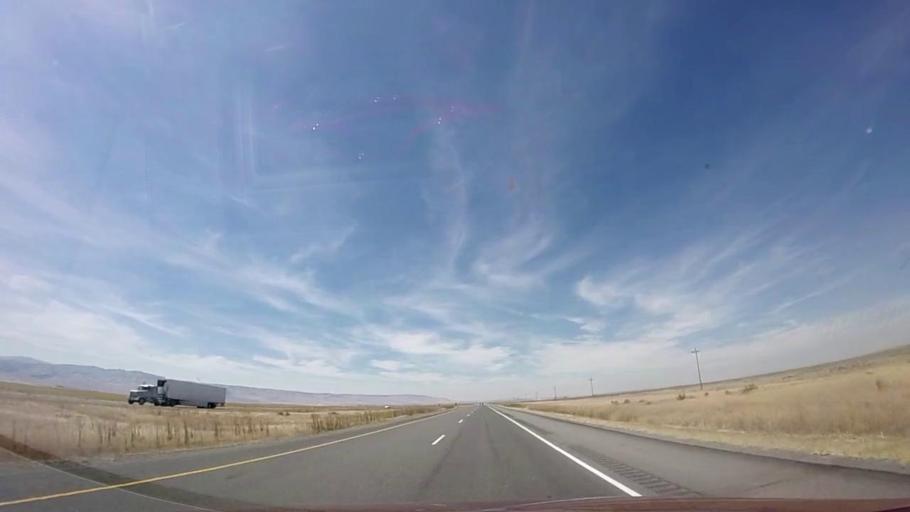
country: US
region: Idaho
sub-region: Minidoka County
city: Rupert
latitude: 42.3496
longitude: -113.2421
